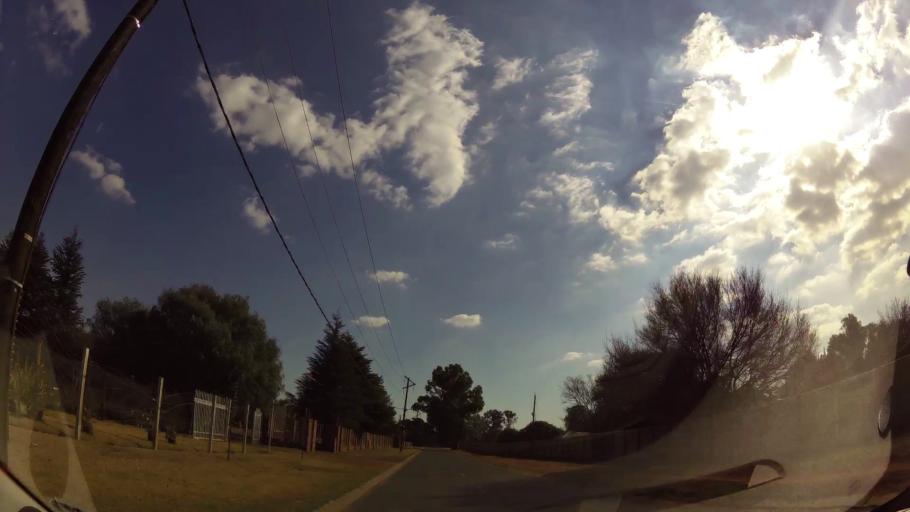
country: ZA
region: Gauteng
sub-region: Ekurhuleni Metropolitan Municipality
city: Benoni
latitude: -26.1142
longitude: 28.3437
